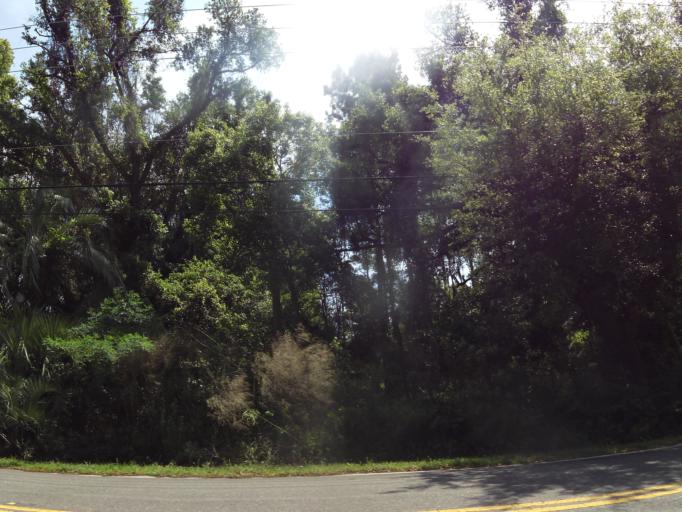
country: US
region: Florida
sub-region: Nassau County
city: Yulee
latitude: 30.5198
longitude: -81.6554
